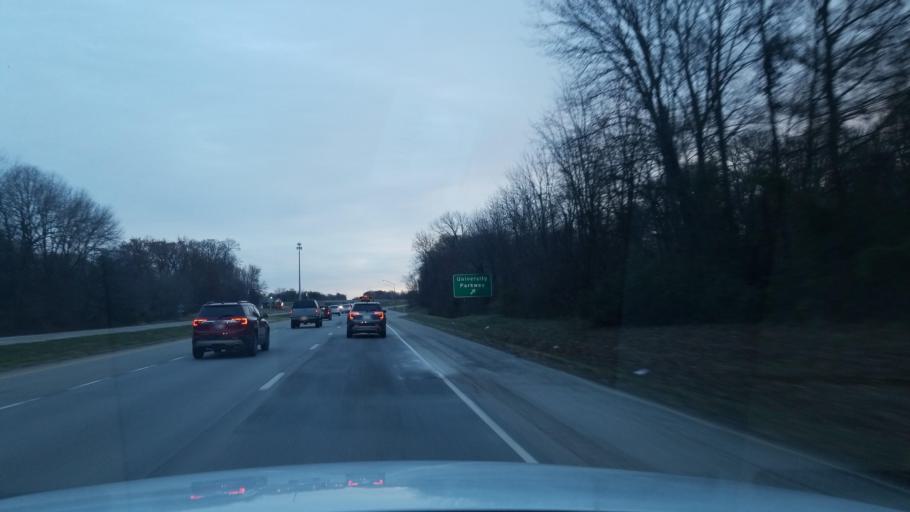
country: US
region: Indiana
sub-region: Vanderburgh County
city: Evansville
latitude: 37.9652
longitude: -87.6850
